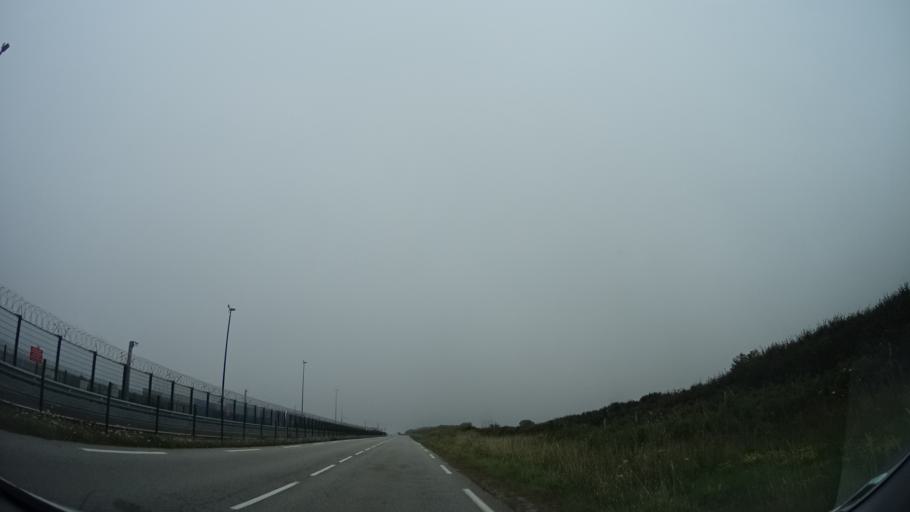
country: FR
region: Lower Normandy
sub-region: Departement de la Manche
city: Flamanville
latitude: 49.5338
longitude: -1.8781
